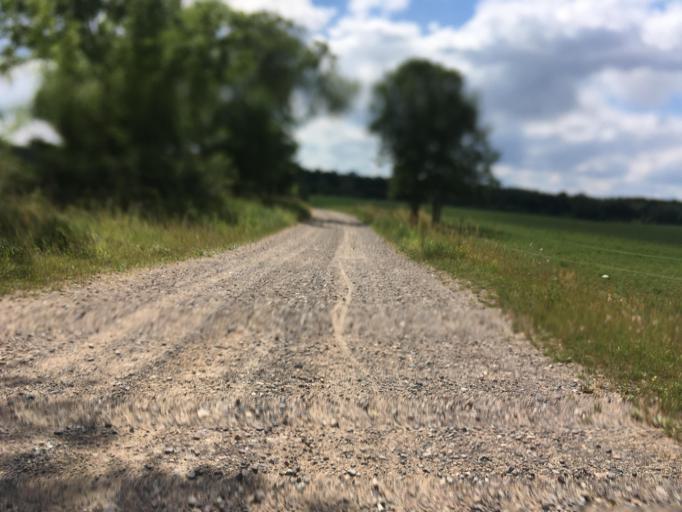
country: DE
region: Brandenburg
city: Althuttendorf
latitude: 52.9556
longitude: 13.8428
